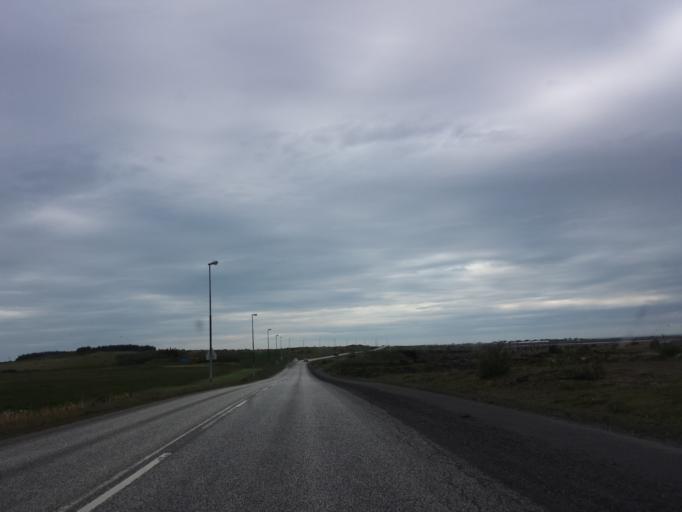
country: IS
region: Capital Region
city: Hafnarfjoerdur
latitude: 64.0852
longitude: -21.9693
